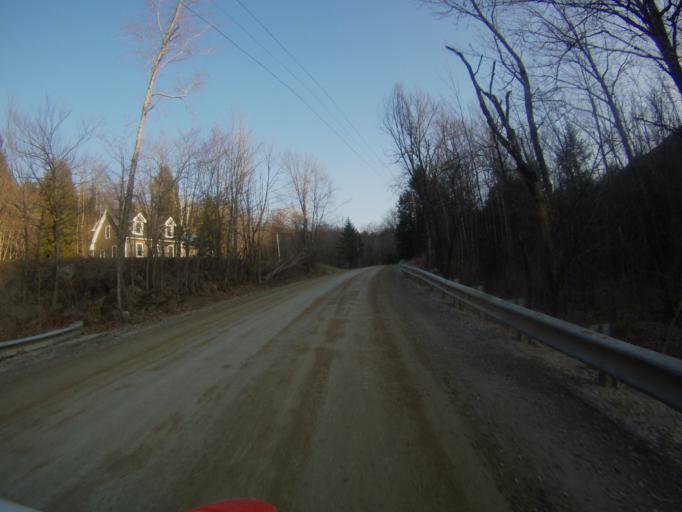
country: US
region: Vermont
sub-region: Addison County
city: Bristol
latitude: 44.0760
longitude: -73.0610
